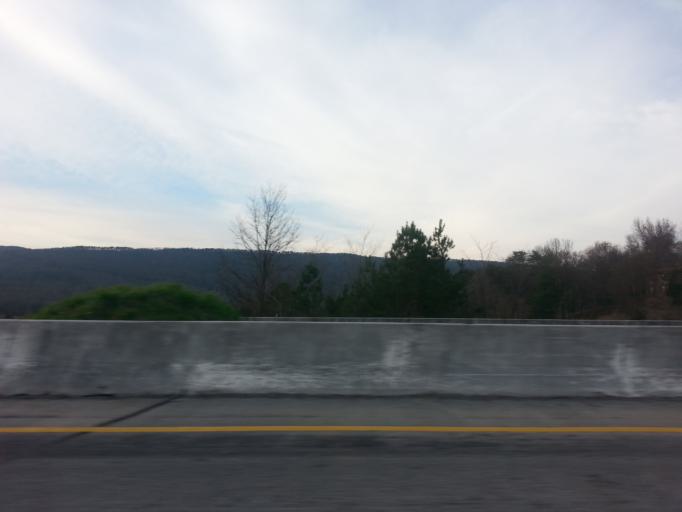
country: US
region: Tennessee
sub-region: Rhea County
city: Dayton
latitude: 35.5577
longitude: -84.9569
